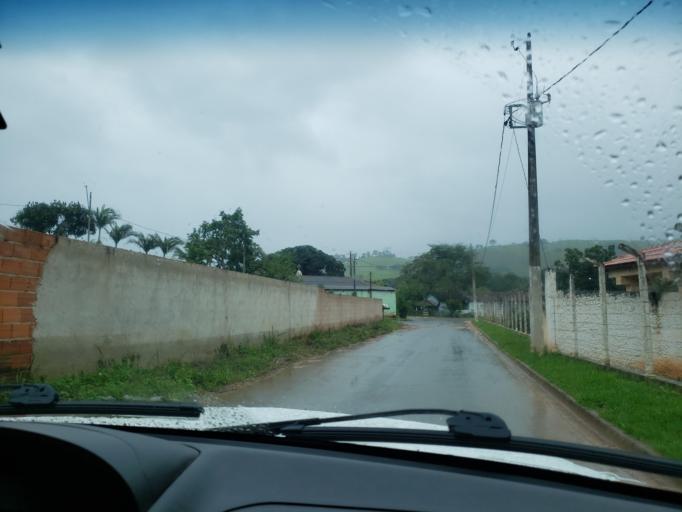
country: BR
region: Minas Gerais
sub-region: Monte Siao
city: Monte Siao
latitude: -22.3792
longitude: -46.5556
